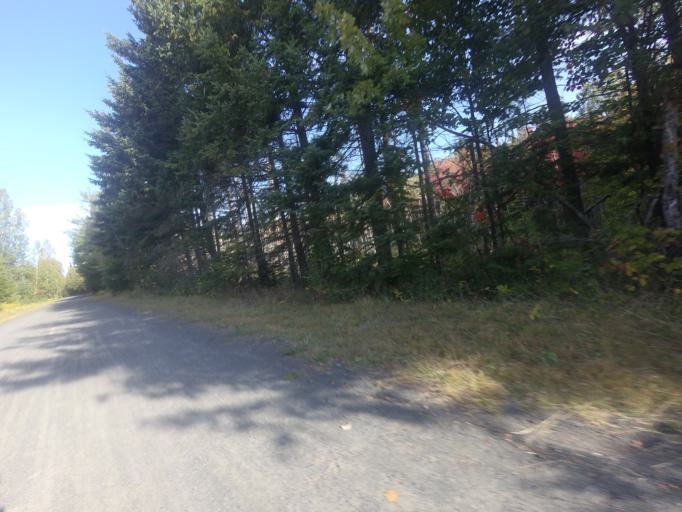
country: CA
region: Quebec
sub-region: Laurentides
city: Val-David
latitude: 46.0118
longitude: -74.1751
